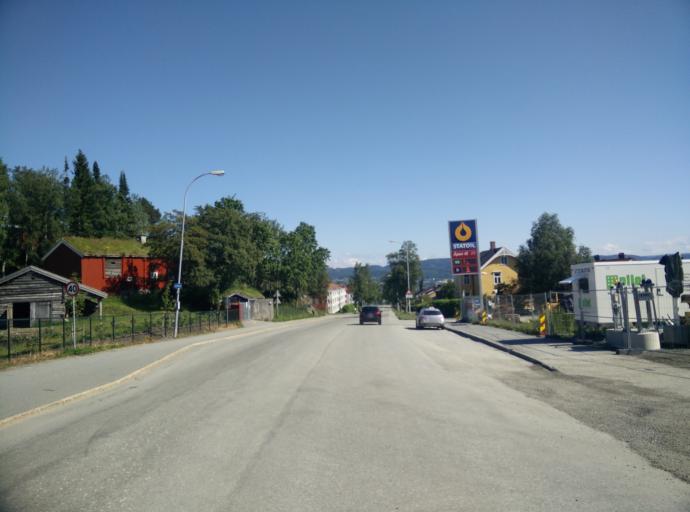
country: NO
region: Sor-Trondelag
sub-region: Trondheim
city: Trondheim
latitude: 63.4176
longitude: 10.3541
